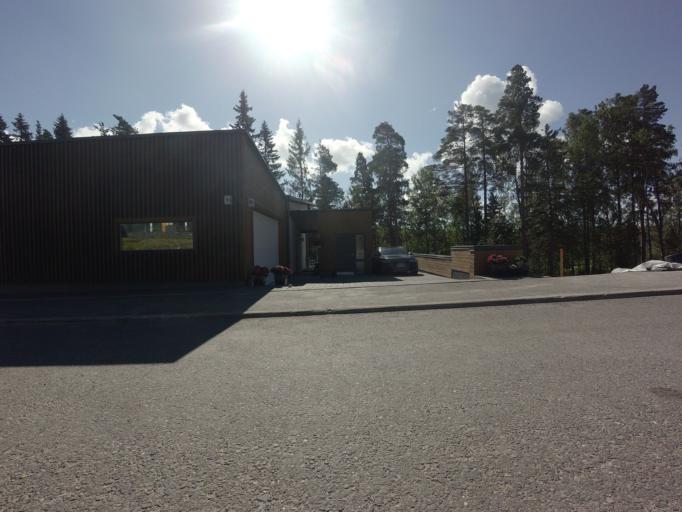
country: FI
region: Uusimaa
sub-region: Helsinki
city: Espoo
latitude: 60.1505
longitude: 24.6022
